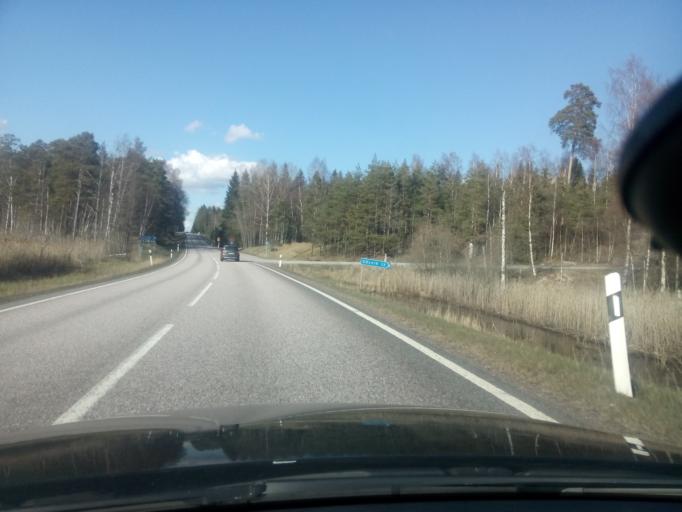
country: SE
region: Soedermanland
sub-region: Strangnas Kommun
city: Akers Styckebruk
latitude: 59.2364
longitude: 16.9371
